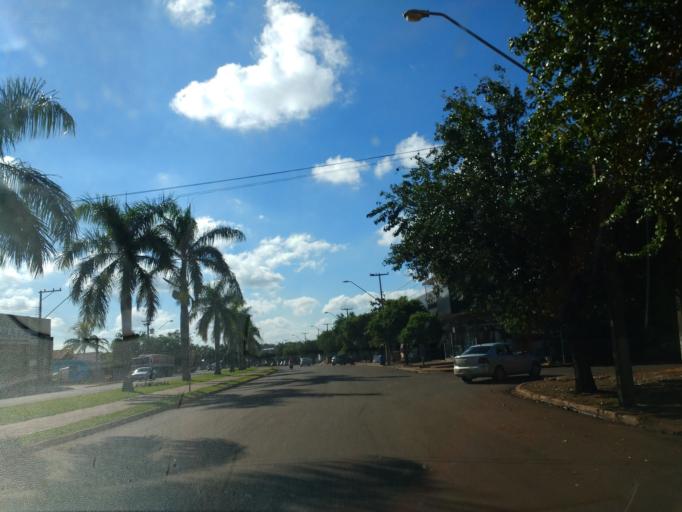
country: BR
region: Parana
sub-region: Palotina
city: Palotina
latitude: -24.3960
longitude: -53.5120
